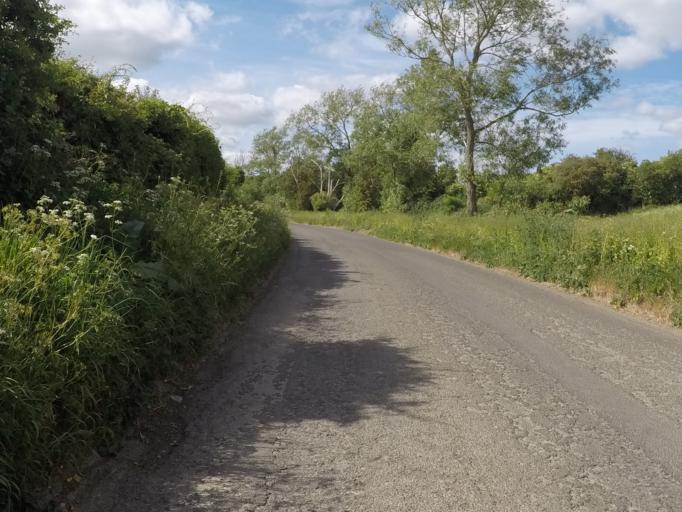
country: GB
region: England
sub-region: Oxfordshire
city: Witney
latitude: 51.8141
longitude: -1.5167
